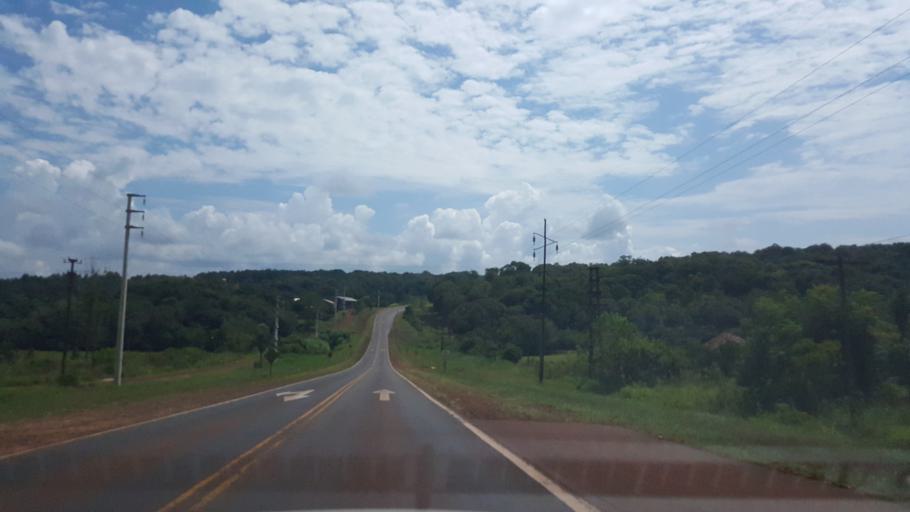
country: AR
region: Misiones
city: Capiovi
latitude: -26.8634
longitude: -55.0451
